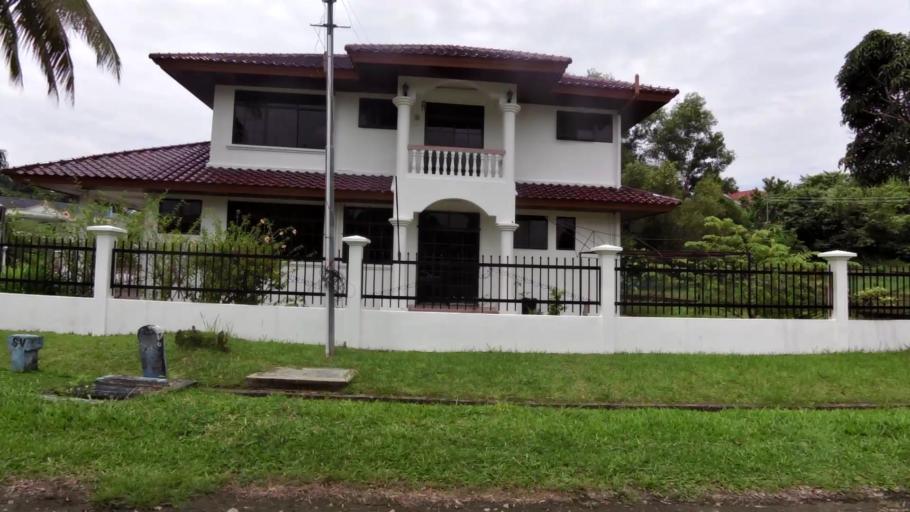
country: BN
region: Brunei and Muara
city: Bandar Seri Begawan
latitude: 4.8943
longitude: 114.9253
